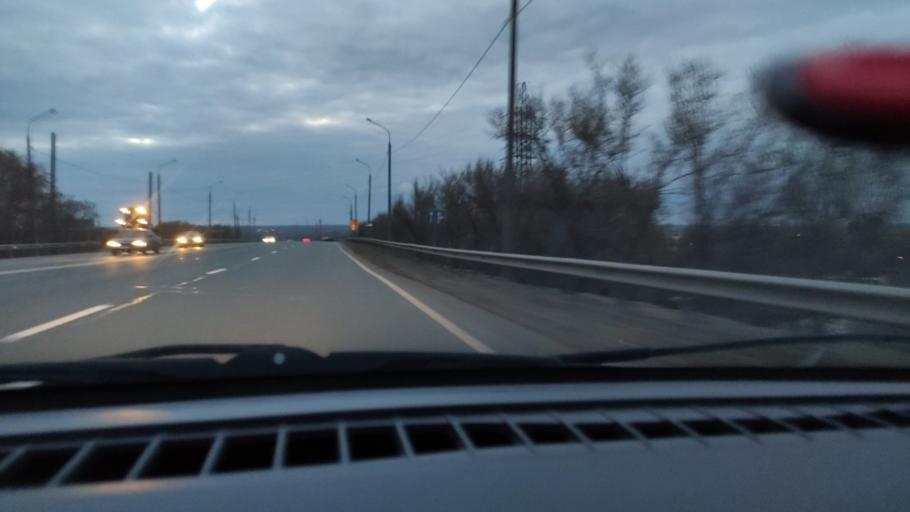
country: RU
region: Orenburg
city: Orenburg
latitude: 51.8541
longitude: 55.1368
